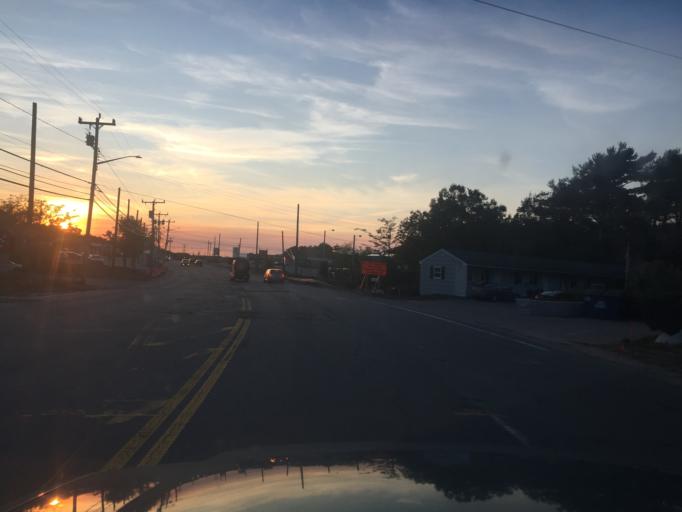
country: US
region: Massachusetts
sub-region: Plymouth County
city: Onset
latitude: 41.7561
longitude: -70.6426
